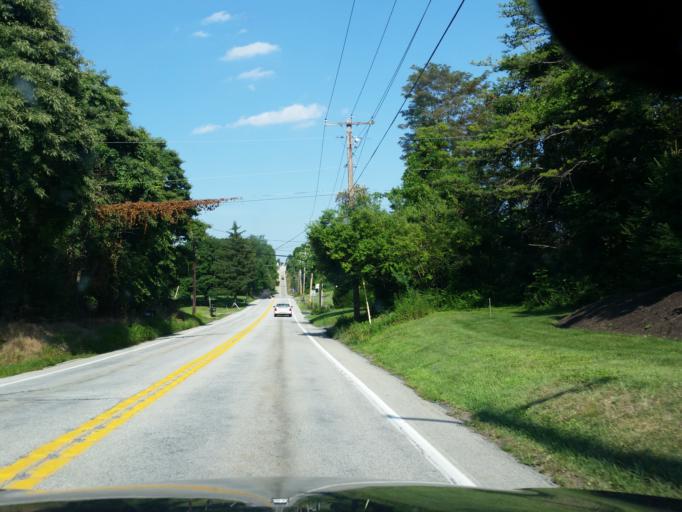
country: US
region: Pennsylvania
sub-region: Cumberland County
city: Mechanicsburg
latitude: 40.2845
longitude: -77.0348
